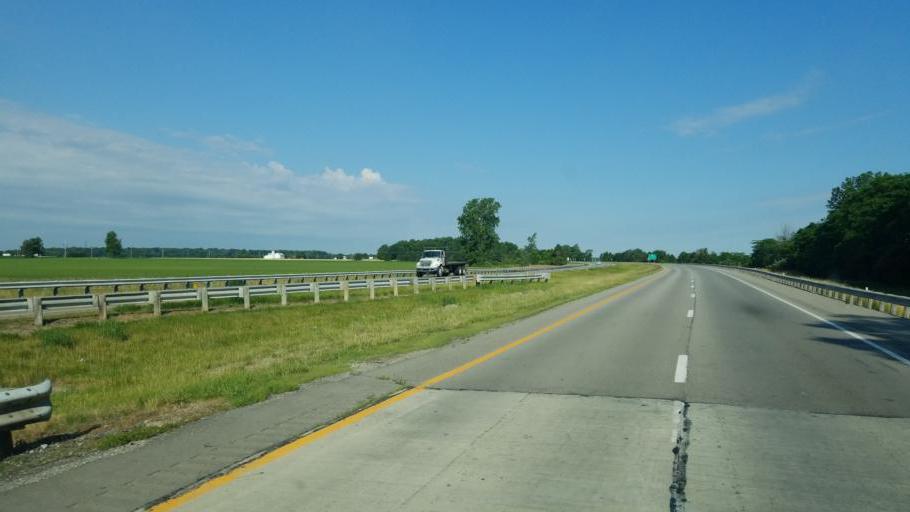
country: US
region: Ohio
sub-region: Hancock County
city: Findlay
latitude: 40.9844
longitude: -83.5567
